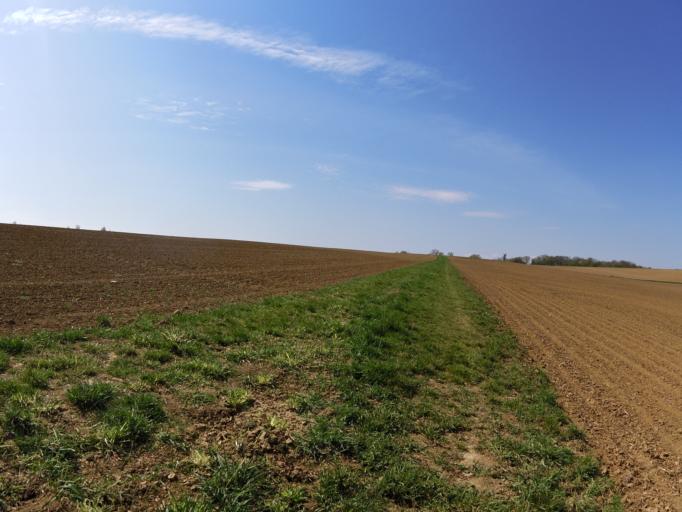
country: DE
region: Bavaria
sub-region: Regierungsbezirk Unterfranken
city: Giebelstadt
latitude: 49.6919
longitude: 9.9622
